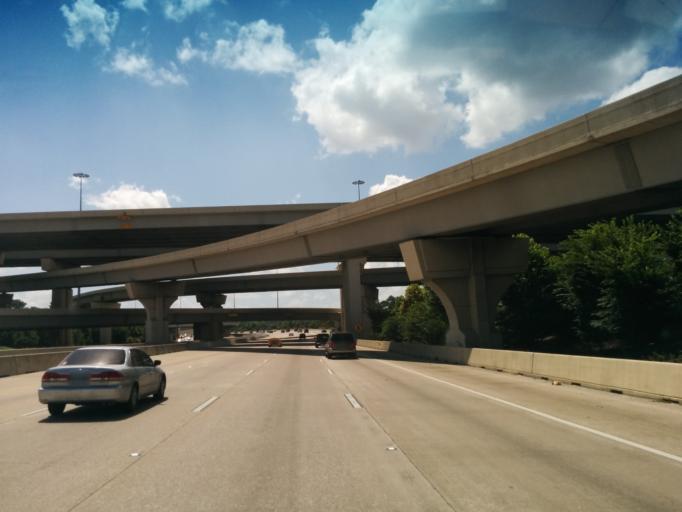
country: US
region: Texas
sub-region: Harris County
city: Hunters Creek Village
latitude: 29.7812
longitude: -95.4552
